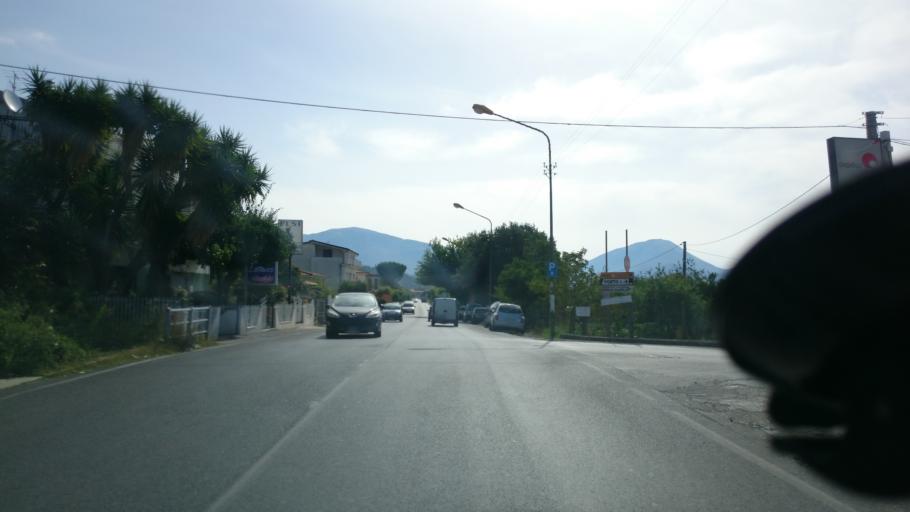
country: IT
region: Campania
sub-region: Provincia di Salerno
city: Policastro Bussentino
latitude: 40.0739
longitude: 15.5228
